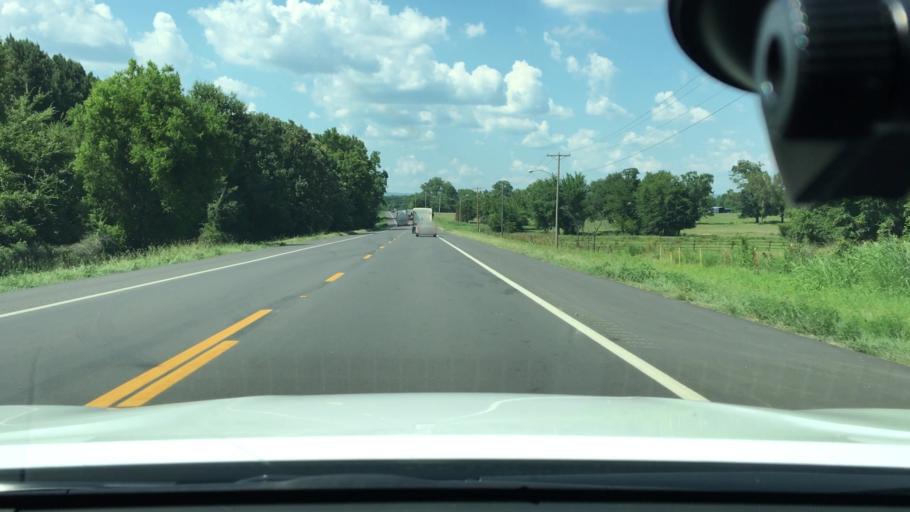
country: US
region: Arkansas
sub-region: Johnson County
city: Clarksville
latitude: 35.4428
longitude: -93.5291
